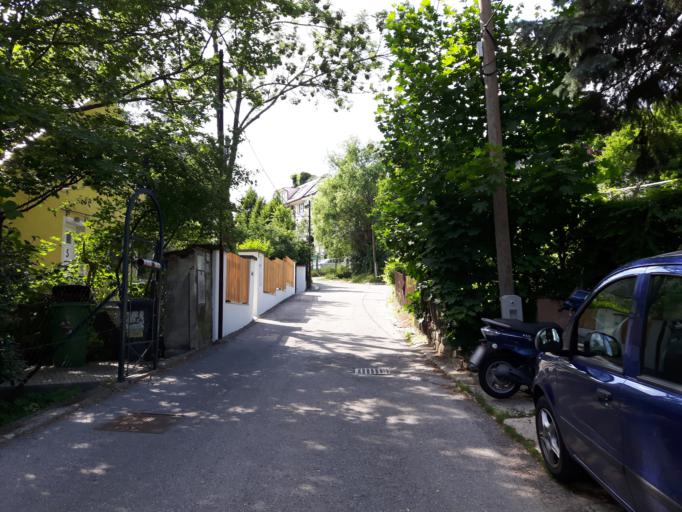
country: AT
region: Lower Austria
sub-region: Politischer Bezirk Wien-Umgebung
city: Klosterneuburg
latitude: 48.2540
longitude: 16.2971
